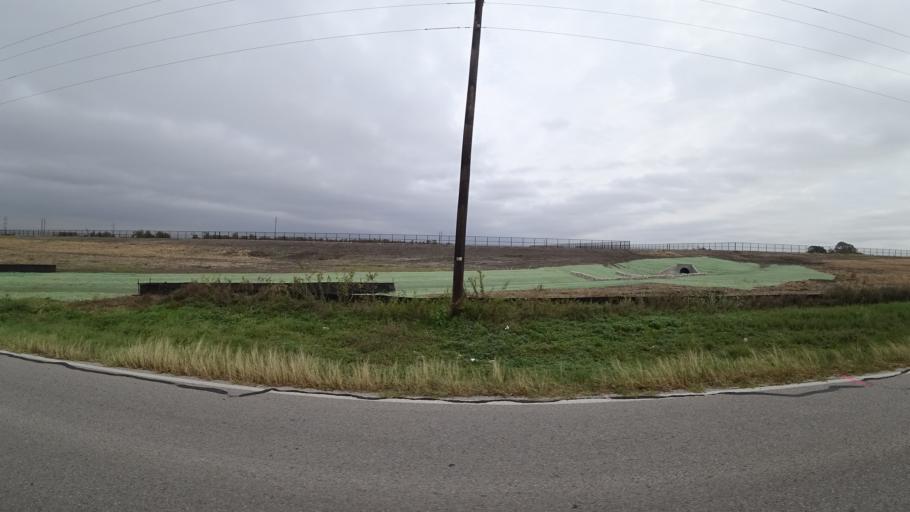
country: US
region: Texas
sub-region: Travis County
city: Manor
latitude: 30.4070
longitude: -97.5592
